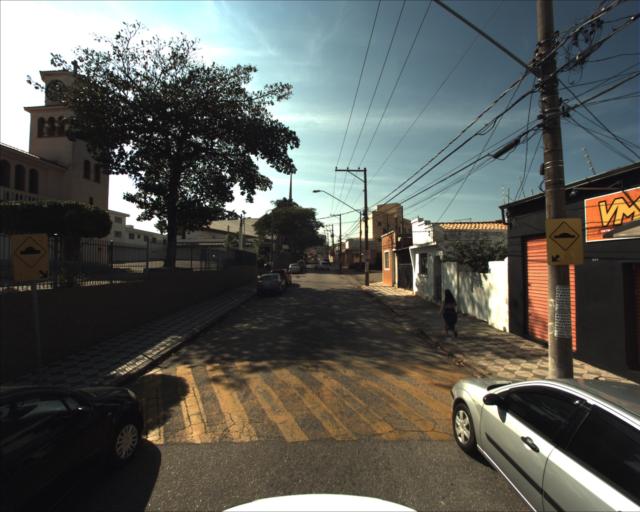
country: BR
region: Sao Paulo
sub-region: Sorocaba
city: Sorocaba
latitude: -23.4871
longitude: -47.4572
